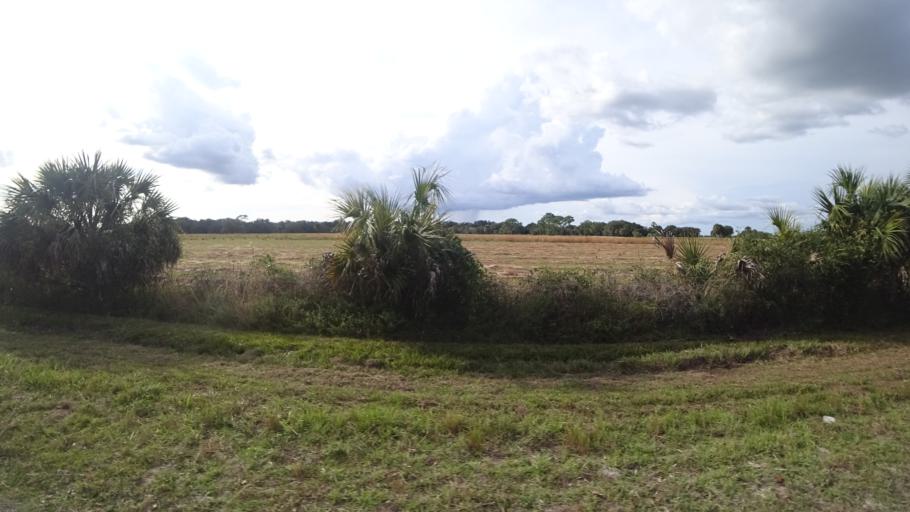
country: US
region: Florida
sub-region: Sarasota County
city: Warm Mineral Springs
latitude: 27.2442
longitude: -82.1667
